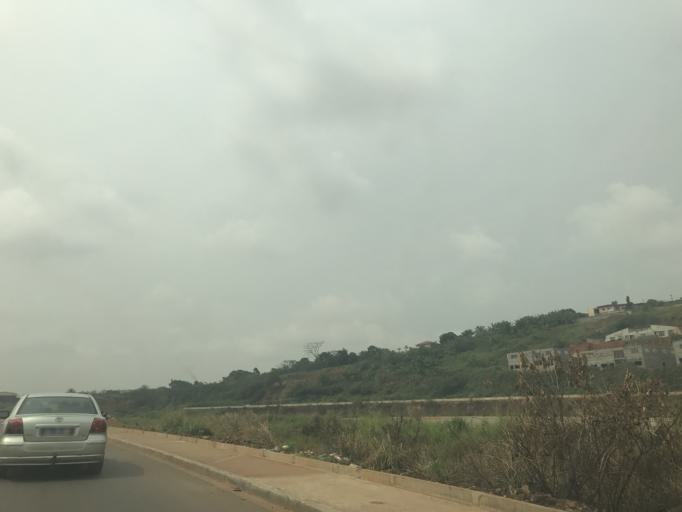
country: CM
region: Centre
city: Yaounde
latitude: 3.8253
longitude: 11.5128
